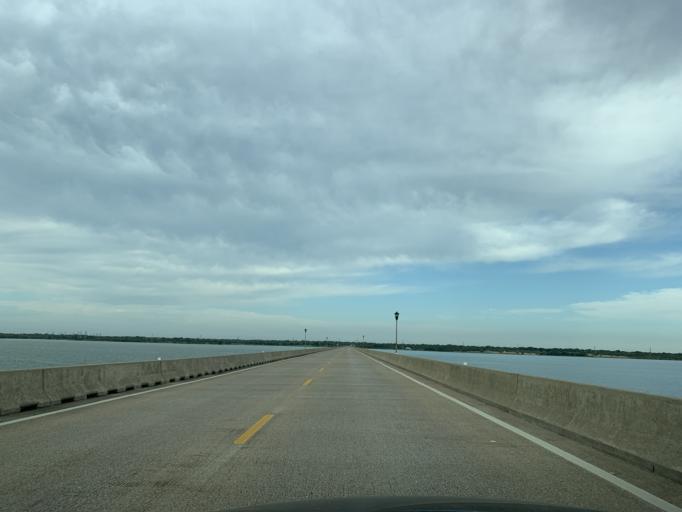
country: US
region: Texas
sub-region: Dallas County
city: Grand Prairie
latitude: 32.7078
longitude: -96.9582
